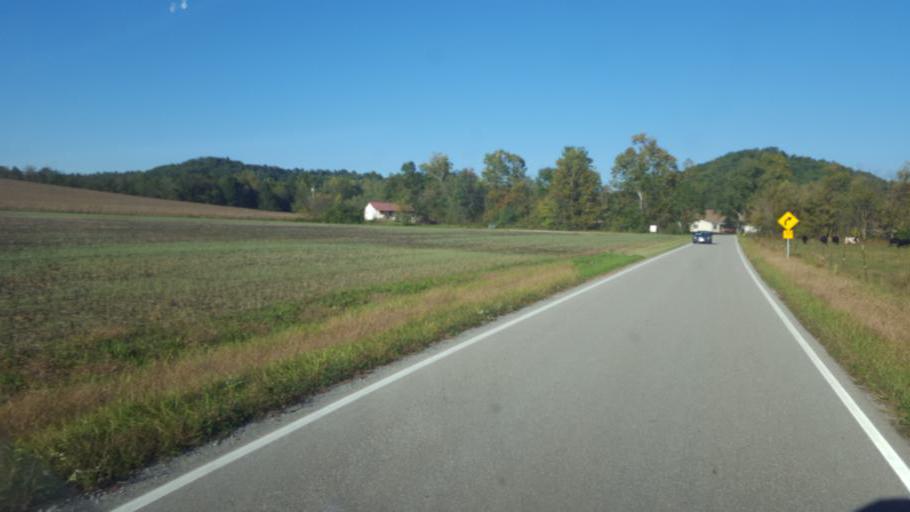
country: US
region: Ohio
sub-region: Adams County
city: Manchester
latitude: 38.5084
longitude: -83.5428
